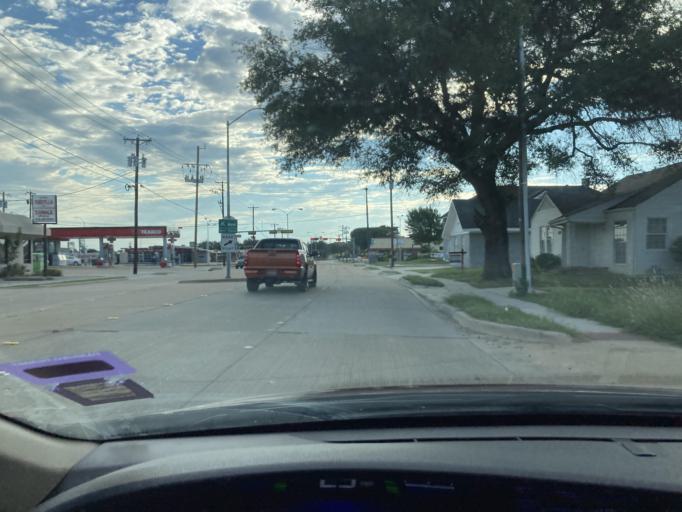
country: US
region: Texas
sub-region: Collin County
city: Plano
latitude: 33.0239
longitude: -96.7004
